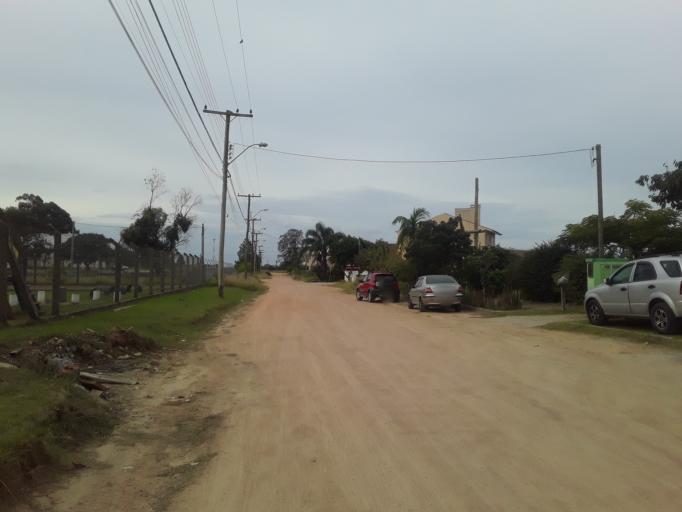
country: BR
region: Rio Grande do Sul
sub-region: Sao Lourenco Do Sul
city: Sao Lourenco do Sul
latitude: -31.3560
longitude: -51.9874
